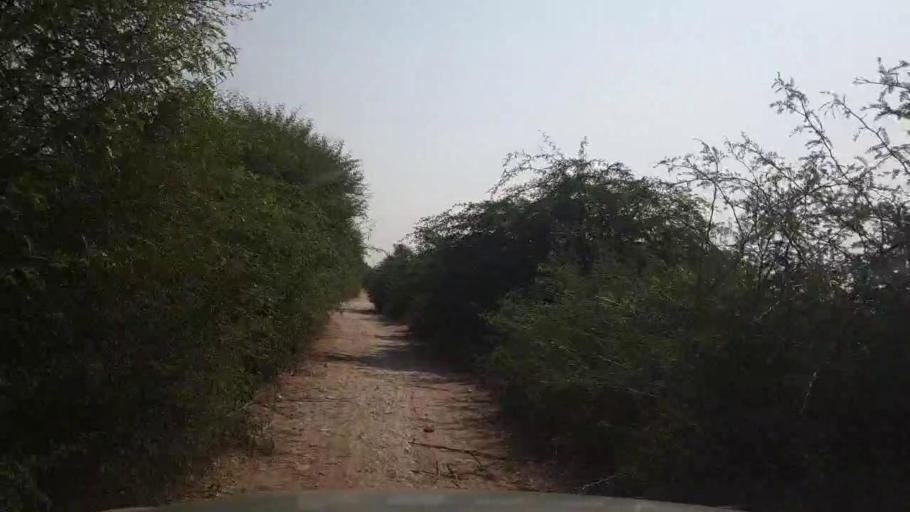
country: PK
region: Sindh
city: Bhit Shah
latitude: 25.7380
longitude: 68.4969
